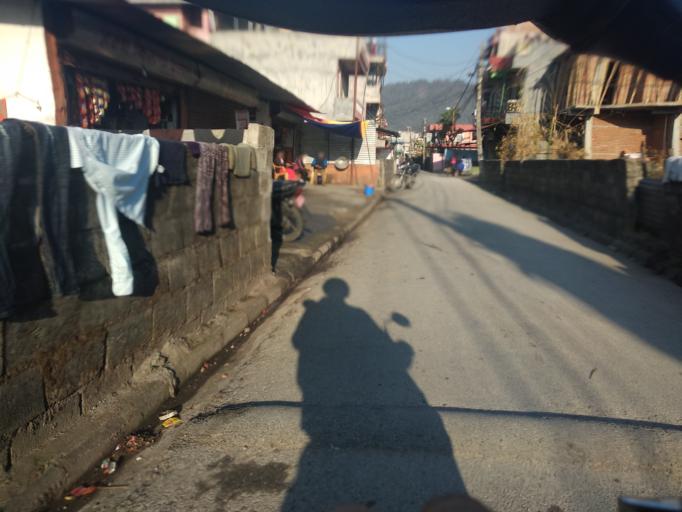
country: NP
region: Western Region
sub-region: Gandaki Zone
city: Pokhara
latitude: 28.2147
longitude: 83.9782
